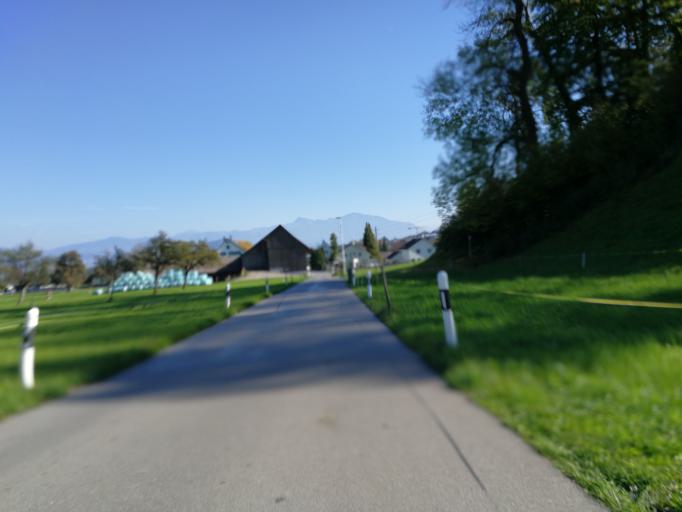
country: CH
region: Schwyz
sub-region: Bezirk March
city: Altendorf
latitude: 47.1943
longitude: 8.8043
